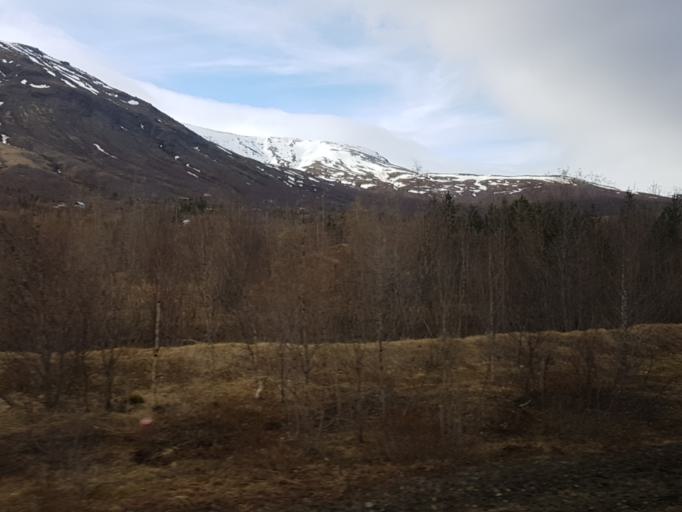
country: IS
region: South
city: Selfoss
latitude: 64.2350
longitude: -20.7074
